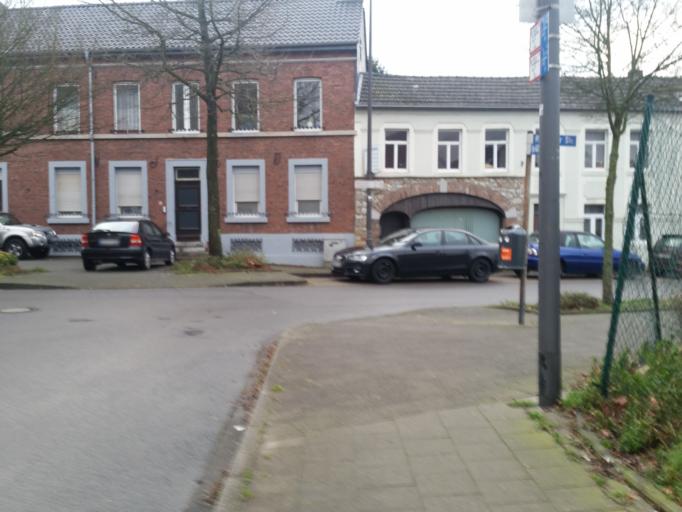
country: DE
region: North Rhine-Westphalia
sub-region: Regierungsbezirk Koln
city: Wurselen
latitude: 50.7844
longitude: 6.1512
